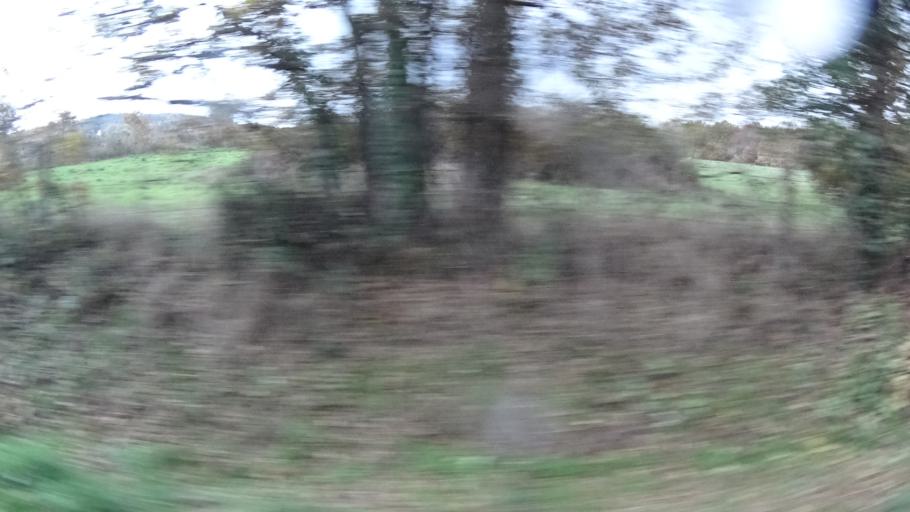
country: FR
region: Pays de la Loire
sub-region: Departement de la Loire-Atlantique
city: Avessac
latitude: 47.6639
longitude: -2.0254
